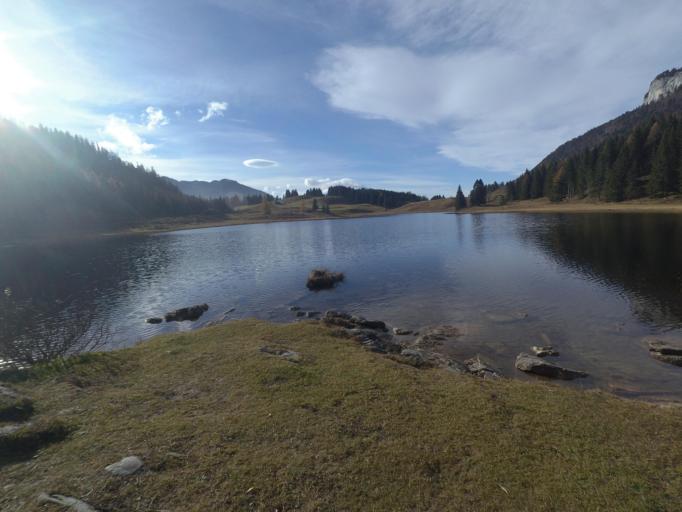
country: AT
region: Salzburg
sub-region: Politischer Bezirk Hallein
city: Scheffau am Tennengebirge
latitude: 47.6275
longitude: 13.2773
